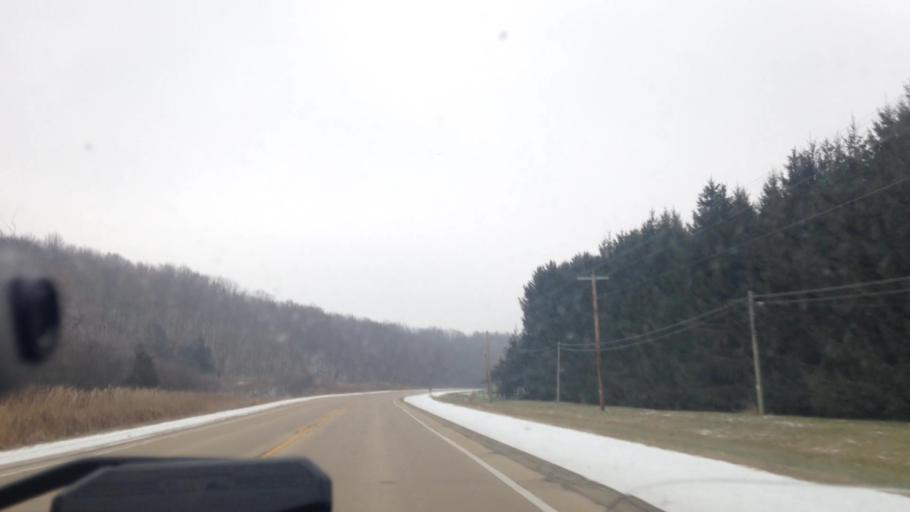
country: US
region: Wisconsin
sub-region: Dodge County
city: Mayville
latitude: 43.4573
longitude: -88.5429
